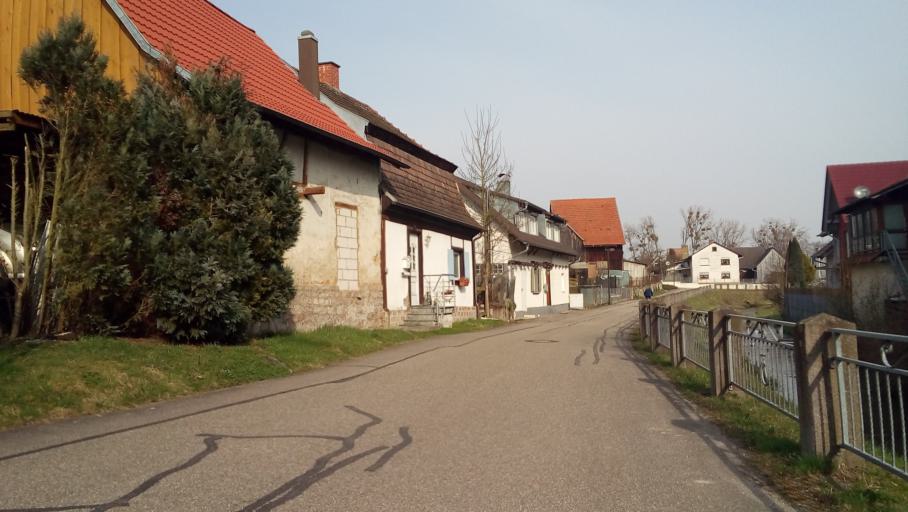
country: DE
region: Baden-Wuerttemberg
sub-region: Freiburg Region
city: Rheinau
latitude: 48.6659
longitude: 7.9340
